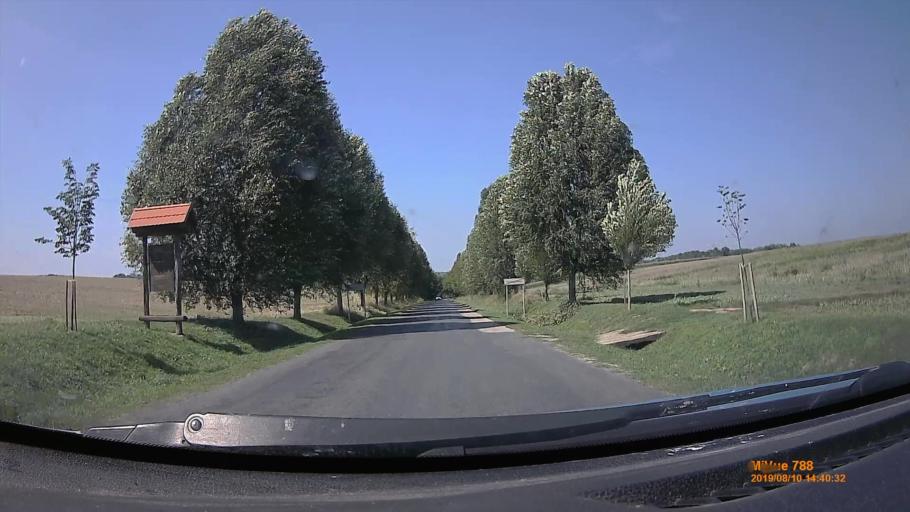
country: HU
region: Somogy
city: Somogyvar
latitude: 46.5758
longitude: 17.6774
